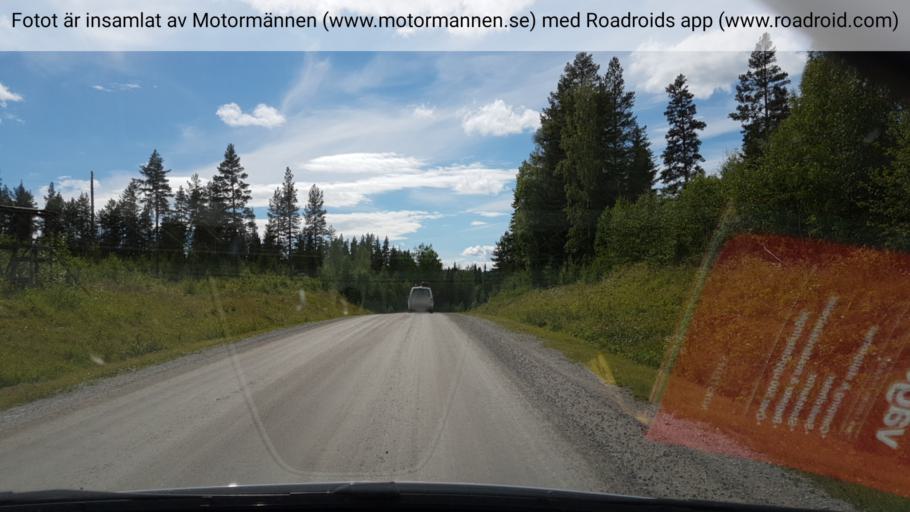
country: SE
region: Vaesternorrland
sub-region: Solleftea Kommun
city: Solleftea
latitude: 63.3155
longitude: 17.2274
